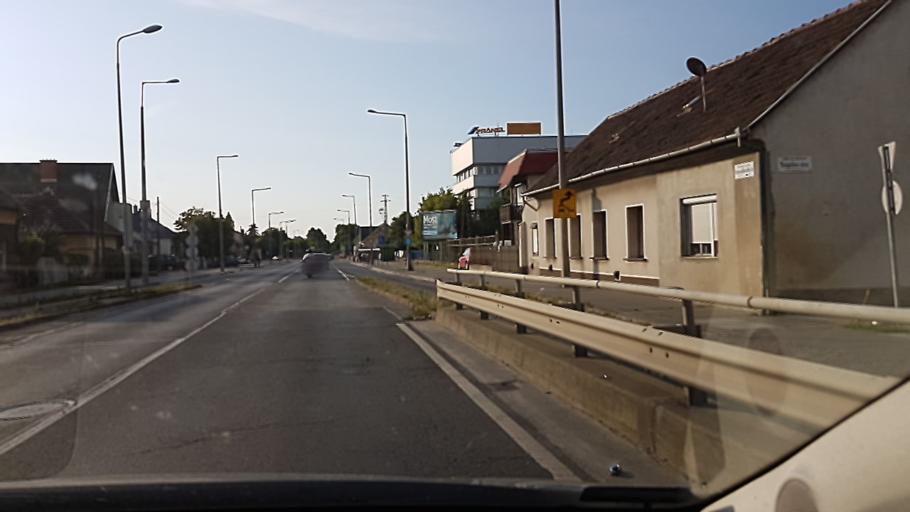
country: HU
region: Budapest
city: Budapest XXIII. keruelet
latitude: 47.3885
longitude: 19.1211
